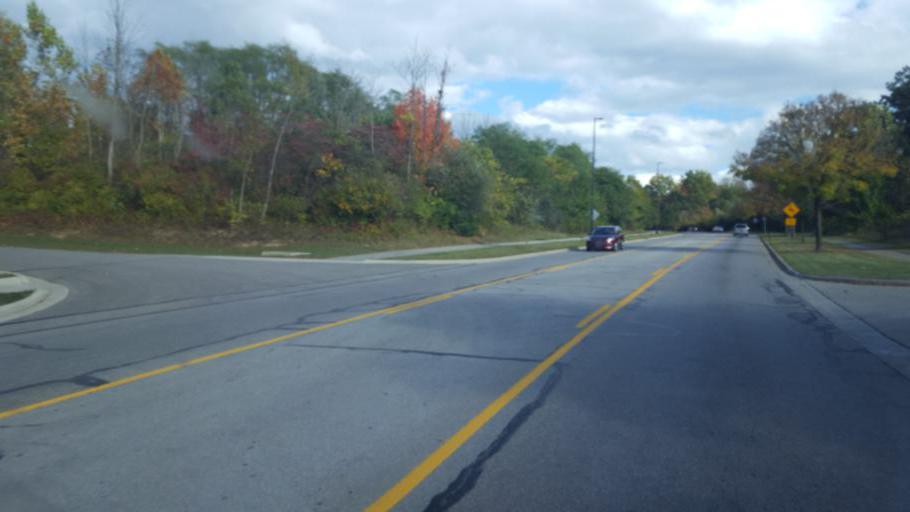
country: US
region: Ohio
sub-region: Franklin County
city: Dublin
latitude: 40.1209
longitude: -83.1079
